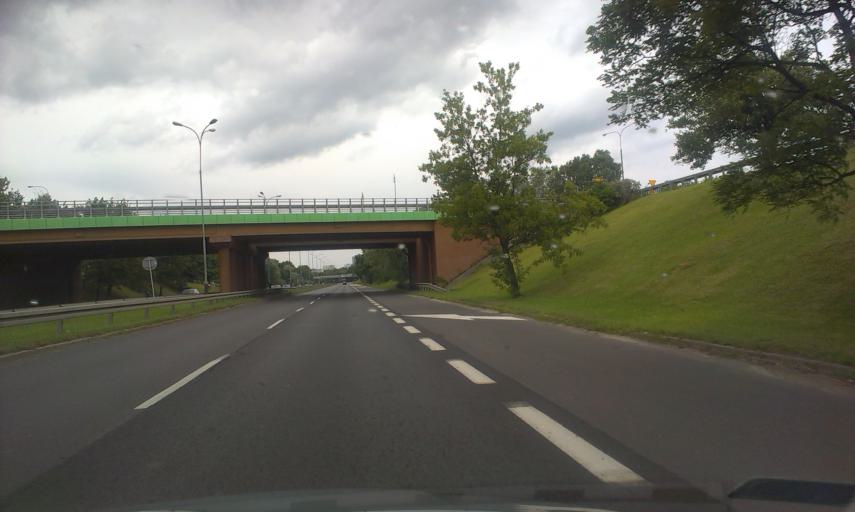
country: PL
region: Greater Poland Voivodeship
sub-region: Poznan
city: Poznan
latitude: 52.4342
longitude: 16.9061
